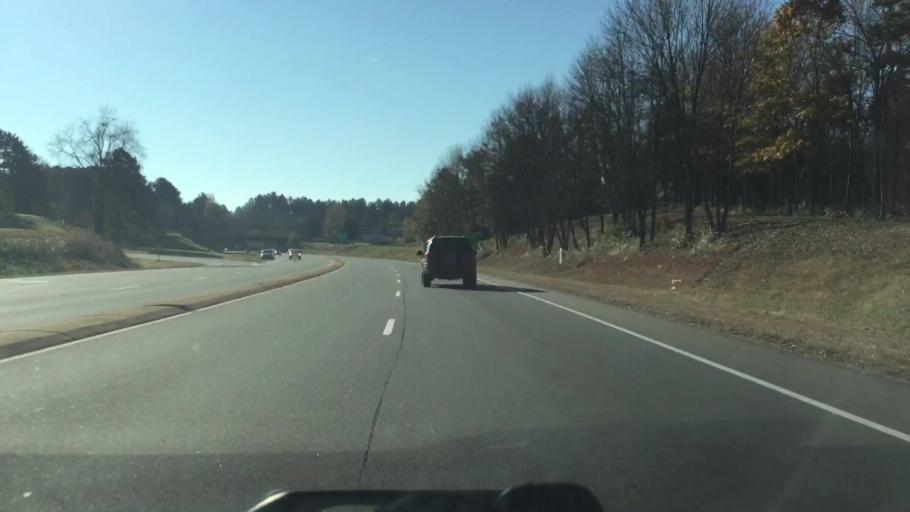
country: US
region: North Carolina
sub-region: Rowan County
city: Salisbury
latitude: 35.6550
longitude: -80.5002
